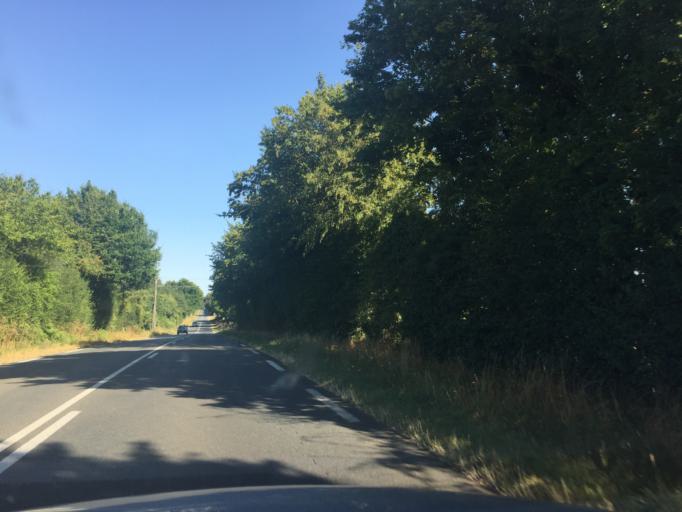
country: FR
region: Poitou-Charentes
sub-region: Departement des Deux-Sevres
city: Chef-Boutonne
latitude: 46.1874
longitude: -0.0450
